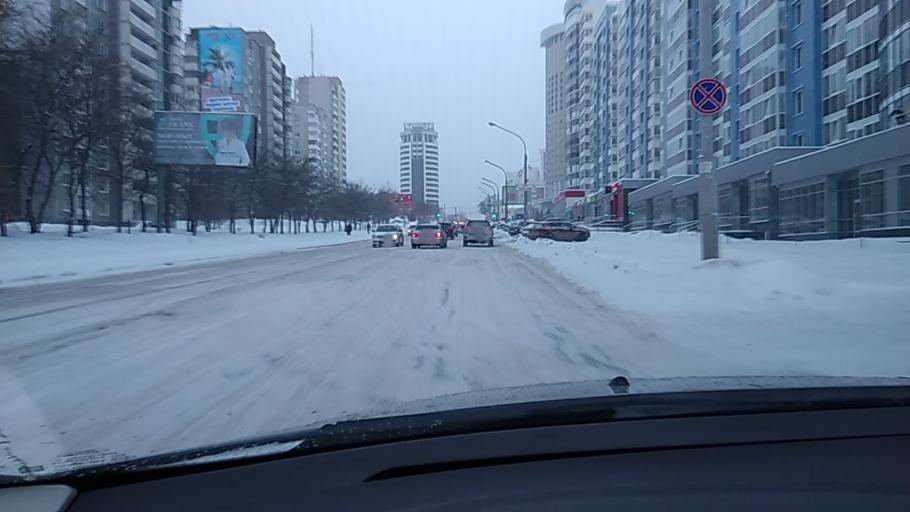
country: RU
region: Sverdlovsk
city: Yekaterinburg
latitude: 56.8260
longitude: 60.5921
